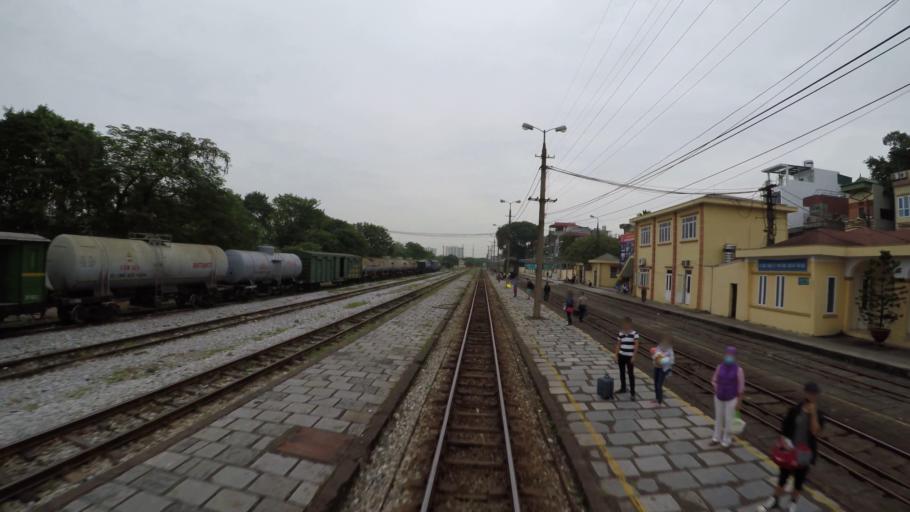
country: VN
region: Ha Noi
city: Trau Quy
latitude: 21.0330
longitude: 105.9070
